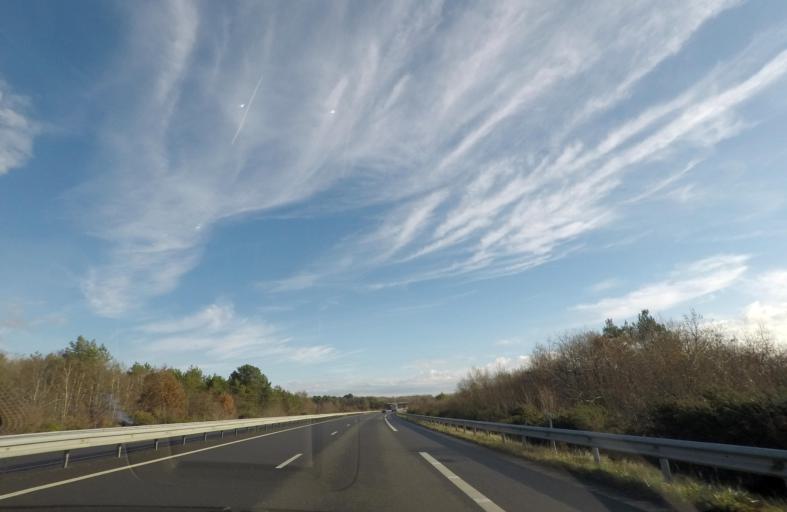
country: FR
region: Centre
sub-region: Departement du Loir-et-Cher
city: Theillay
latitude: 47.2907
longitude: 2.0082
